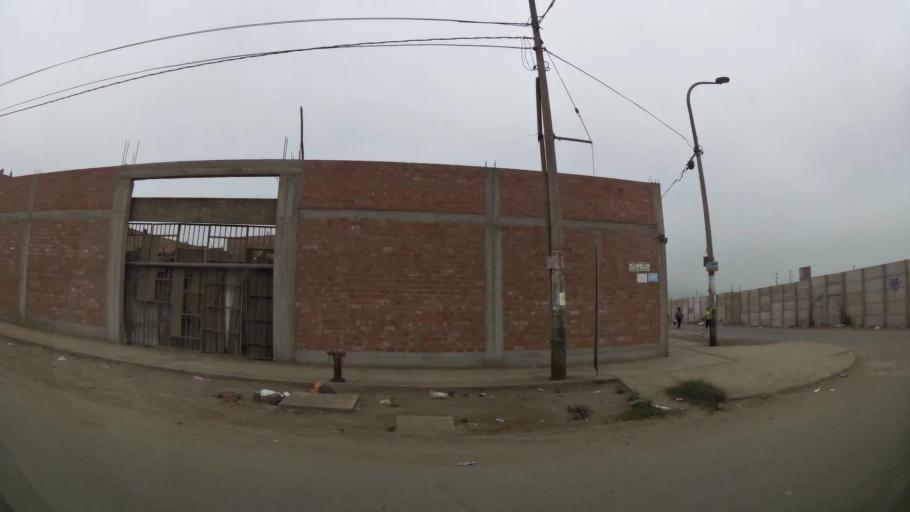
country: PE
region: Lima
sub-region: Lima
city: Urb. Santo Domingo
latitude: -11.8889
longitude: -77.0427
